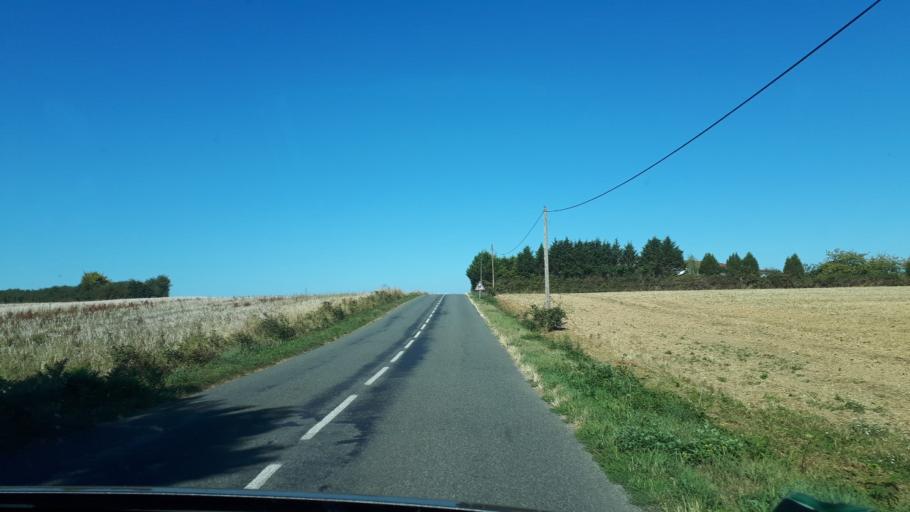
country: FR
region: Centre
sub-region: Departement du Loiret
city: Autry-le-Chatel
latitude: 47.6076
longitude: 2.5719
